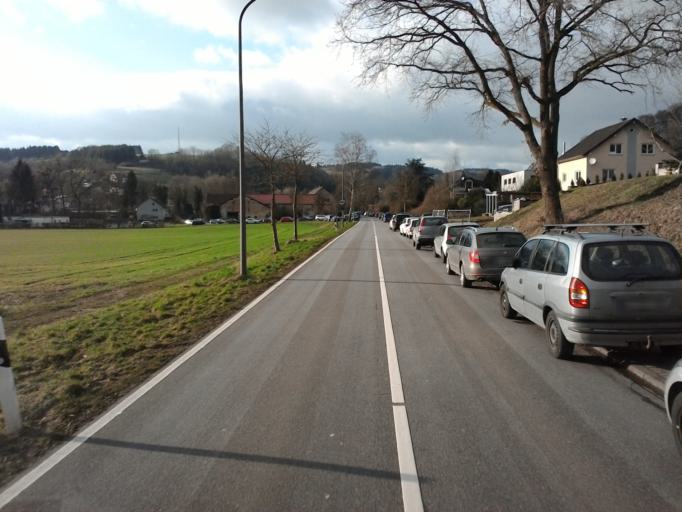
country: DE
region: Rheinland-Pfalz
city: Mettendorf
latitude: 49.9421
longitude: 6.3400
